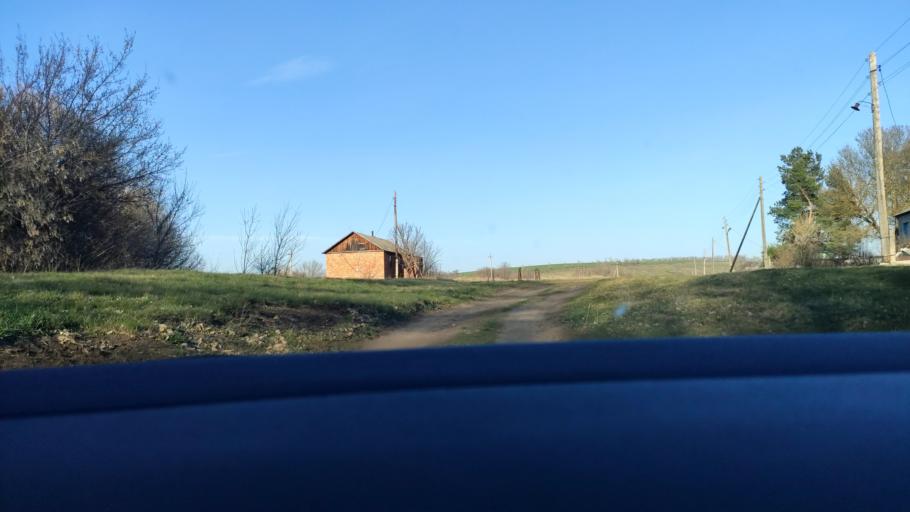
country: RU
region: Voronezj
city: Uryv-Pokrovka
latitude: 51.1474
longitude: 39.0189
